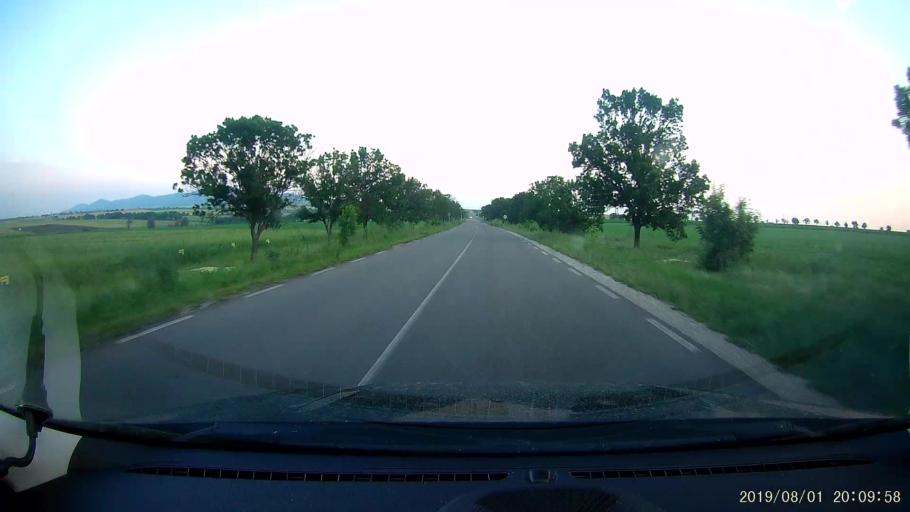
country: BG
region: Yambol
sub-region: Obshtina Yambol
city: Yambol
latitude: 42.4893
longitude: 26.5954
